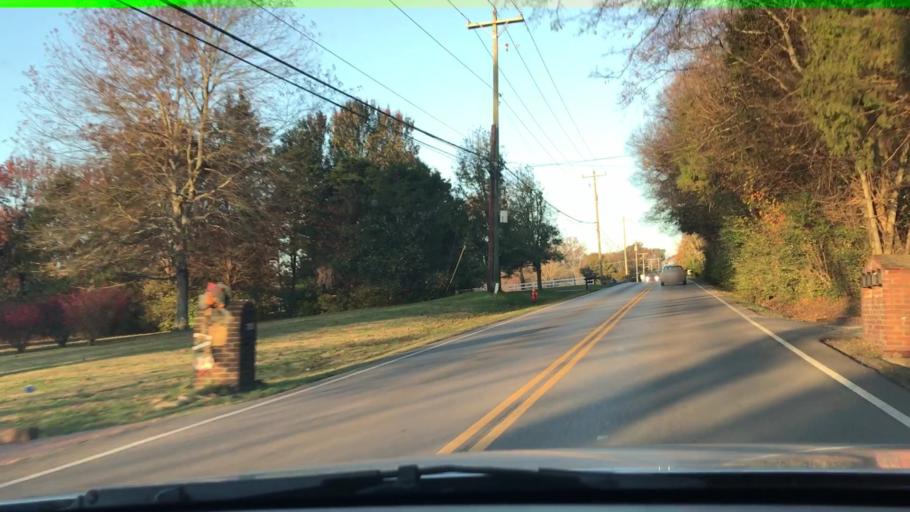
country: US
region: Tennessee
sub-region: Williamson County
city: Brentwood Estates
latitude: 36.0137
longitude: -86.7160
